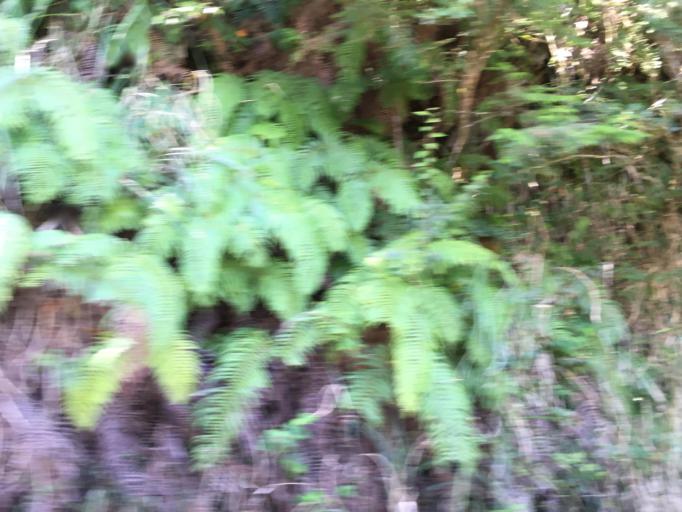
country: TW
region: Taiwan
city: Daxi
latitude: 24.5305
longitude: 121.4012
